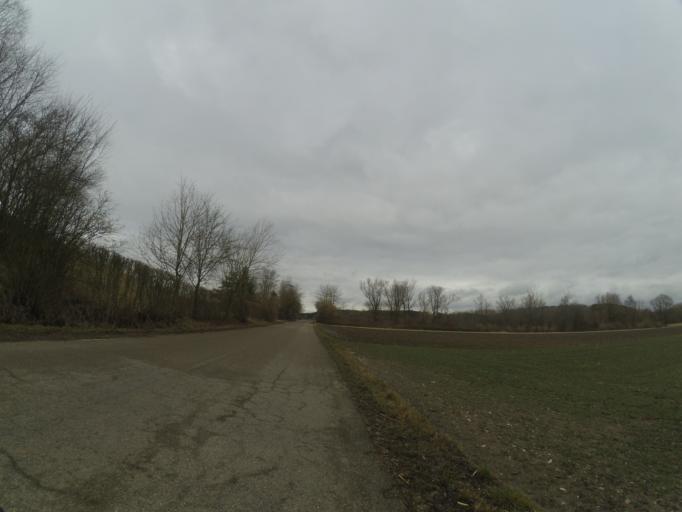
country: DE
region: Bavaria
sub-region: Swabia
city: Vohringen
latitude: 48.2947
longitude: 10.0864
